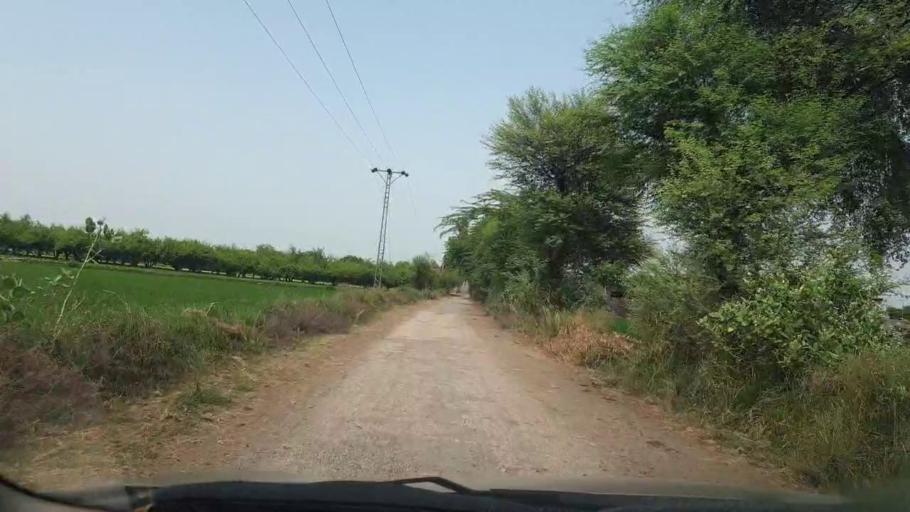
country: PK
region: Sindh
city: Larkana
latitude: 27.5861
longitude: 68.1449
